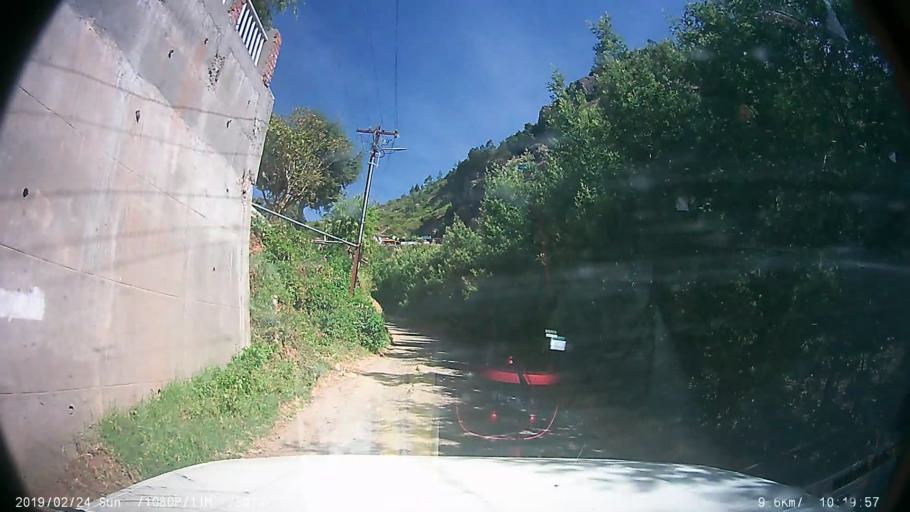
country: IN
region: Tamil Nadu
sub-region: Nilgiri
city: Ooty
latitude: 11.3880
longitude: 76.7200
